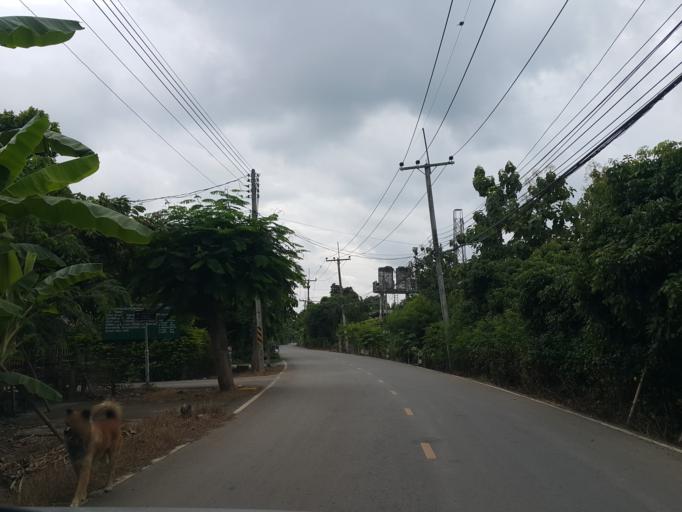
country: TH
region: Chiang Mai
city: San Kamphaeng
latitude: 18.7938
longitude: 99.1315
